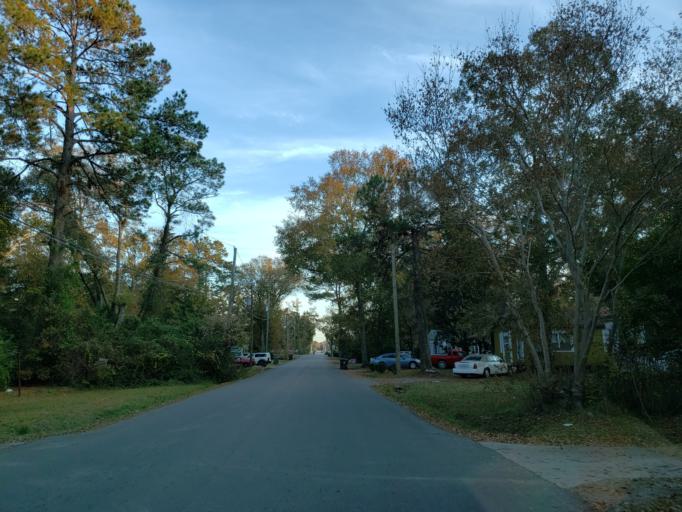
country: US
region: Mississippi
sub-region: Forrest County
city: Hattiesburg
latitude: 31.3171
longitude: -89.3130
